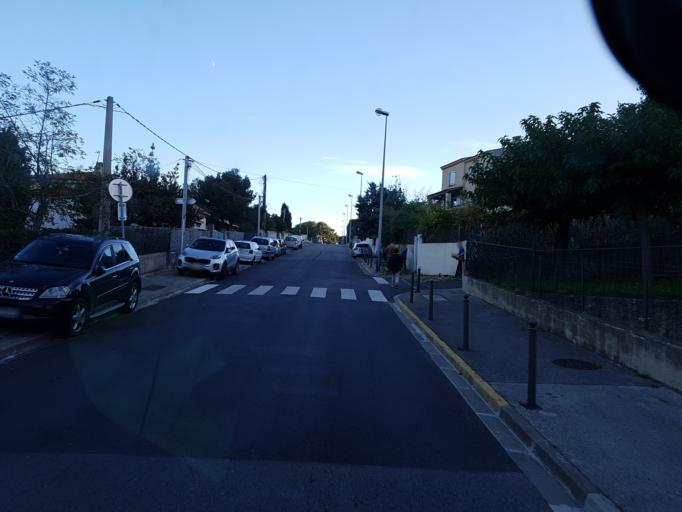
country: FR
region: Provence-Alpes-Cote d'Azur
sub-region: Departement des Bouches-du-Rhone
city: La Ciotat
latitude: 43.1750
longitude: 5.5979
